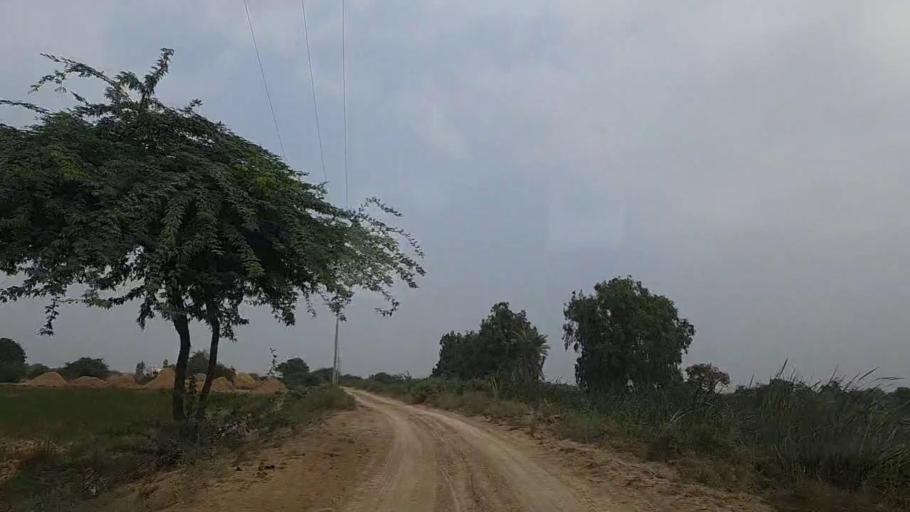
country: PK
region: Sindh
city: Mirpur Sakro
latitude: 24.6110
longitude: 67.7149
